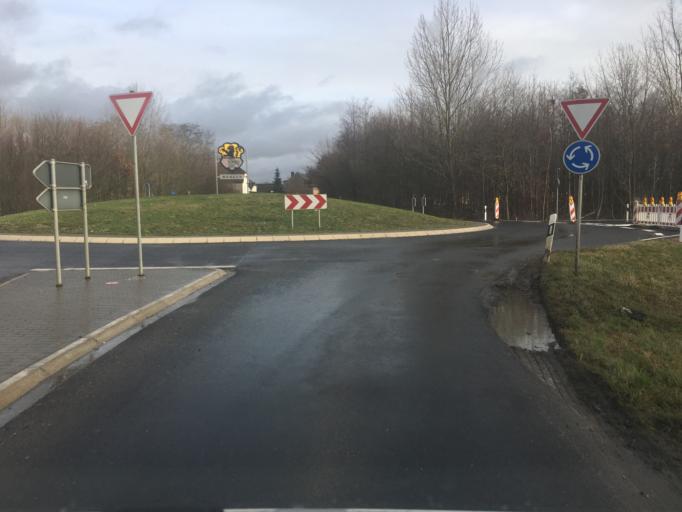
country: DE
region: North Rhine-Westphalia
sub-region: Regierungsbezirk Koln
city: Inden
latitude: 50.8432
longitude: 6.4168
